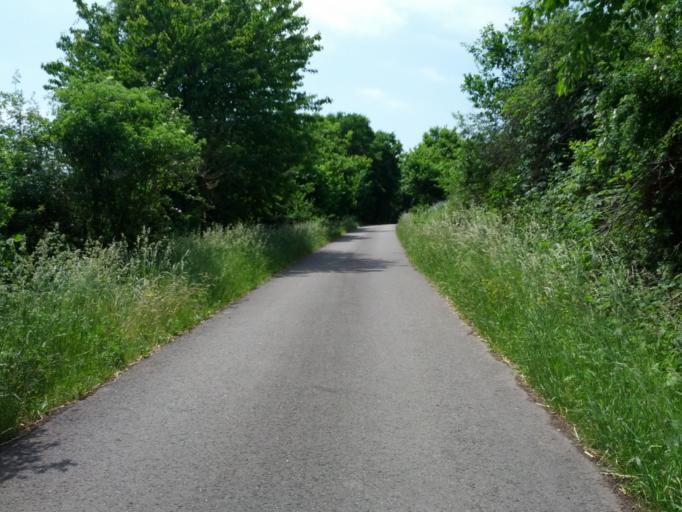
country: DE
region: Thuringia
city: Urnshausen
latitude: 50.7249
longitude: 10.1649
